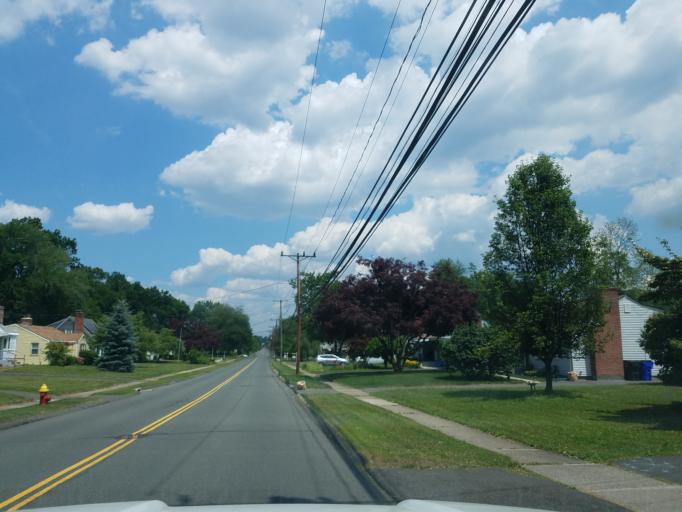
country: US
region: Connecticut
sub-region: Hartford County
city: West Hartford
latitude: 41.7332
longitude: -72.7568
